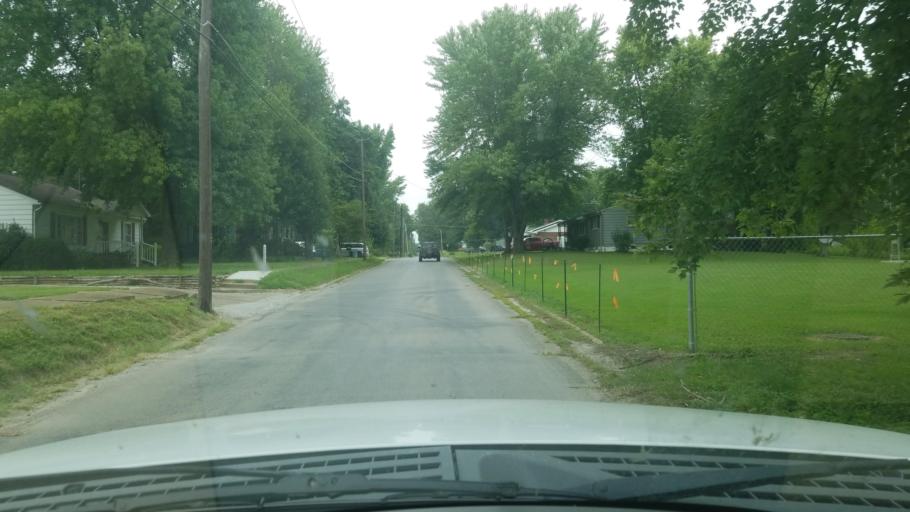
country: US
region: Illinois
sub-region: Saline County
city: Eldorado
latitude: 37.8186
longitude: -88.4475
